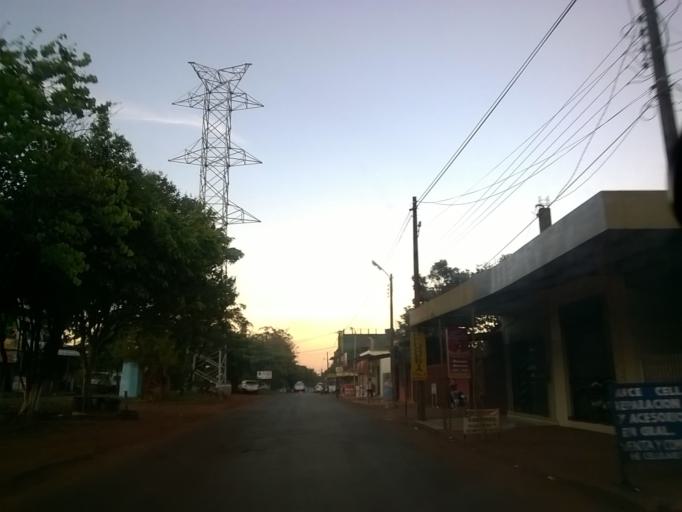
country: PY
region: Alto Parana
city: Ciudad del Este
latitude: -25.4870
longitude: -54.6465
